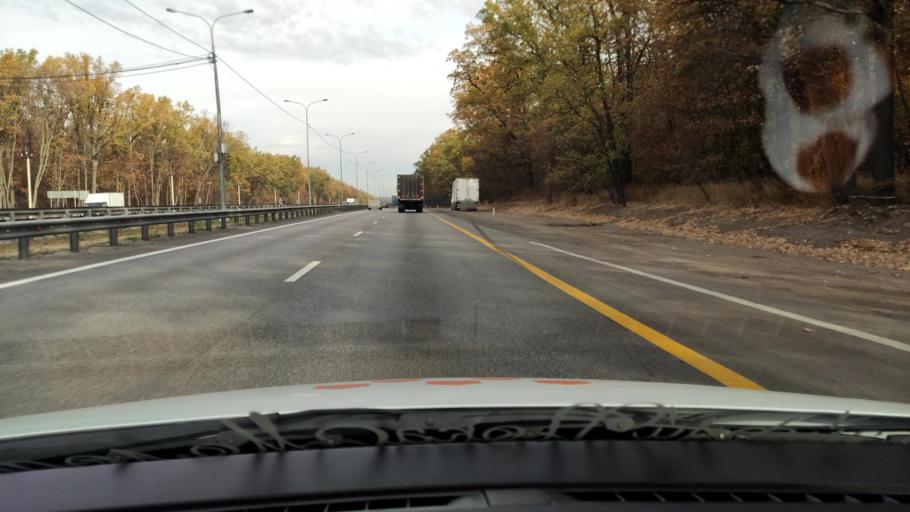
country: RU
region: Voronezj
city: Ramon'
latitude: 51.8572
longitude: 39.2155
